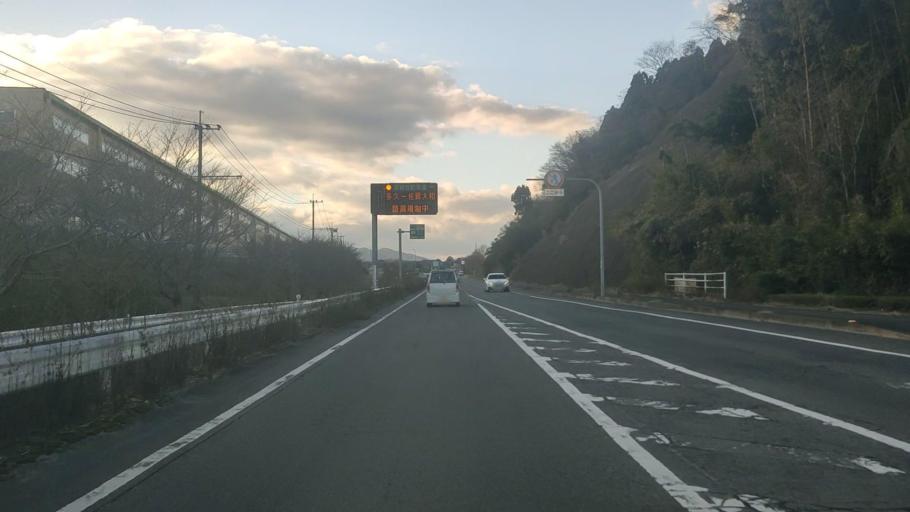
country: JP
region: Saga Prefecture
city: Takeocho-takeo
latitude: 33.2896
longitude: 130.1290
